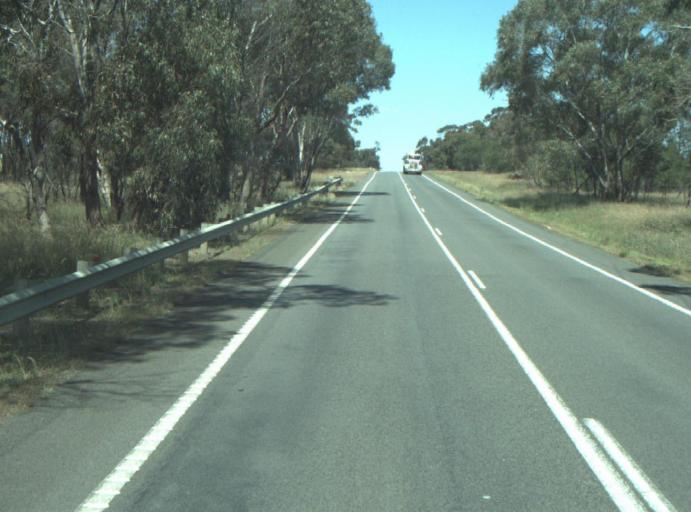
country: AU
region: Victoria
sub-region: Greater Geelong
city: Lara
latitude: -37.9169
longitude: 144.3662
